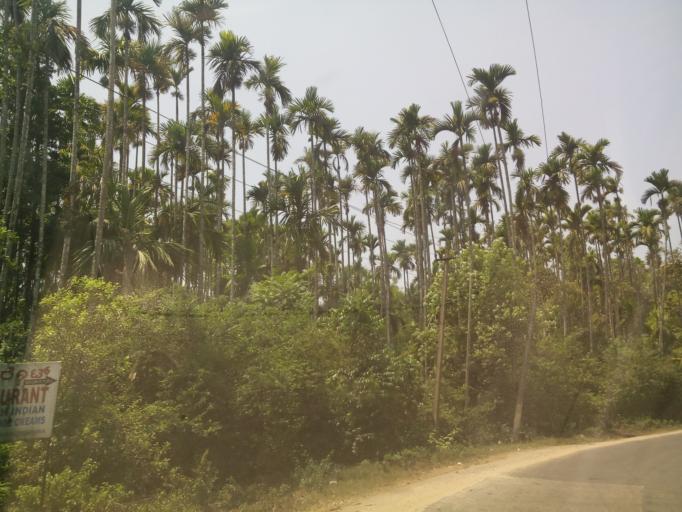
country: IN
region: Karnataka
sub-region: Hassan
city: Sakleshpur
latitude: 12.9473
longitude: 75.8117
